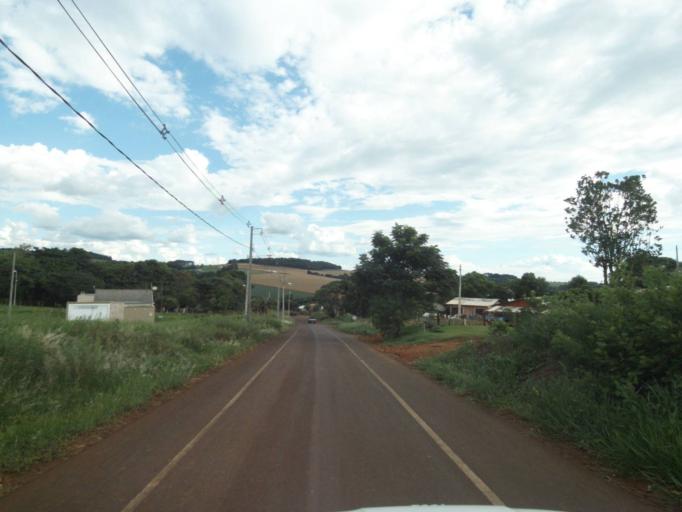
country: BR
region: Parana
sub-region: Laranjeiras Do Sul
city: Laranjeiras do Sul
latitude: -25.4963
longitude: -52.5270
